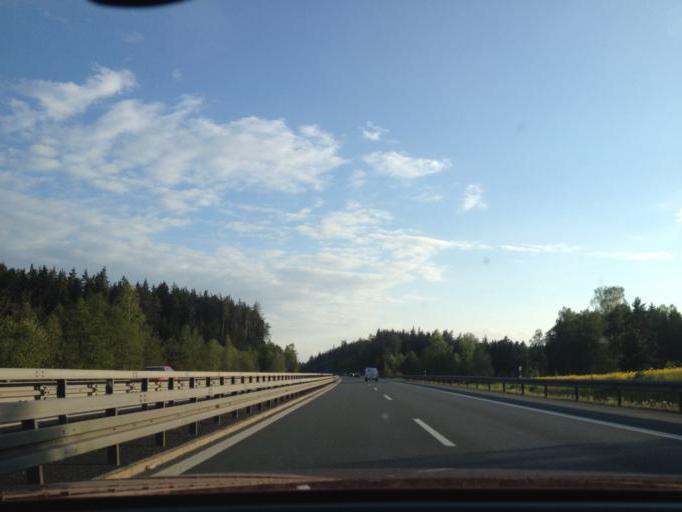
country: DE
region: Bavaria
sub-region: Upper Palatinate
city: Wiesau
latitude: 49.8729
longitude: 12.1908
